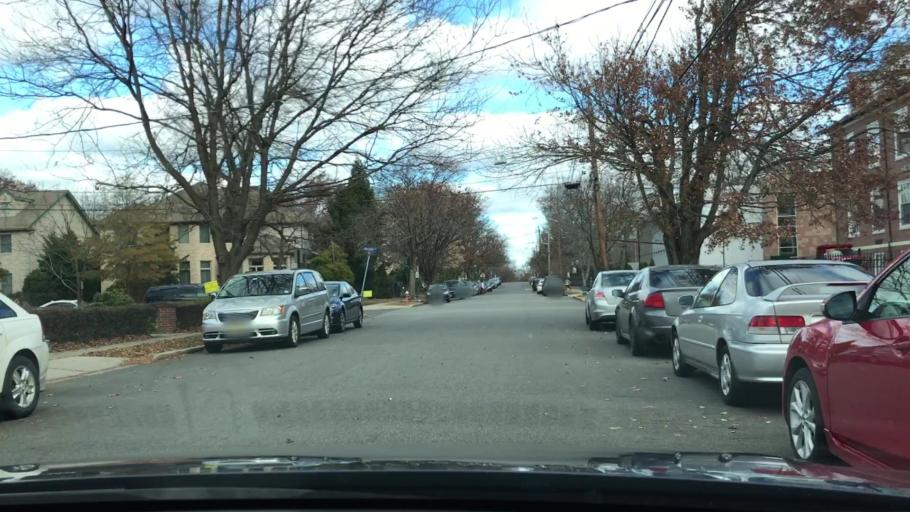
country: US
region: New Jersey
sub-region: Bergen County
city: Rutherford
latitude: 40.8305
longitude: -74.1134
